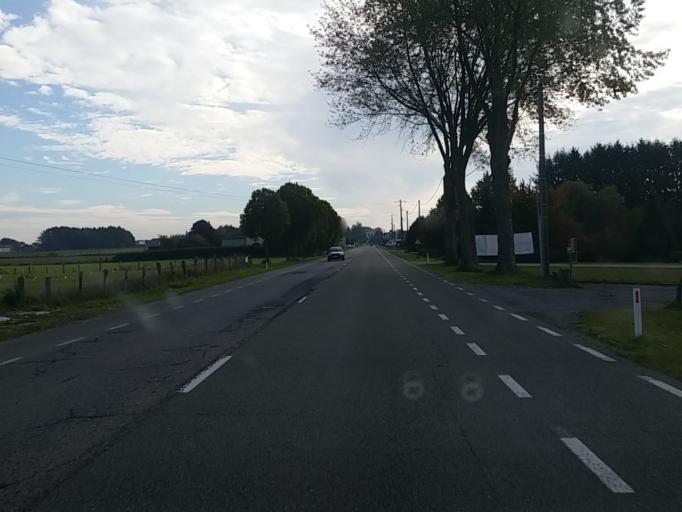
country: BE
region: Wallonia
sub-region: Province du Luxembourg
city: Florenville
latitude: 49.6982
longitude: 5.2903
